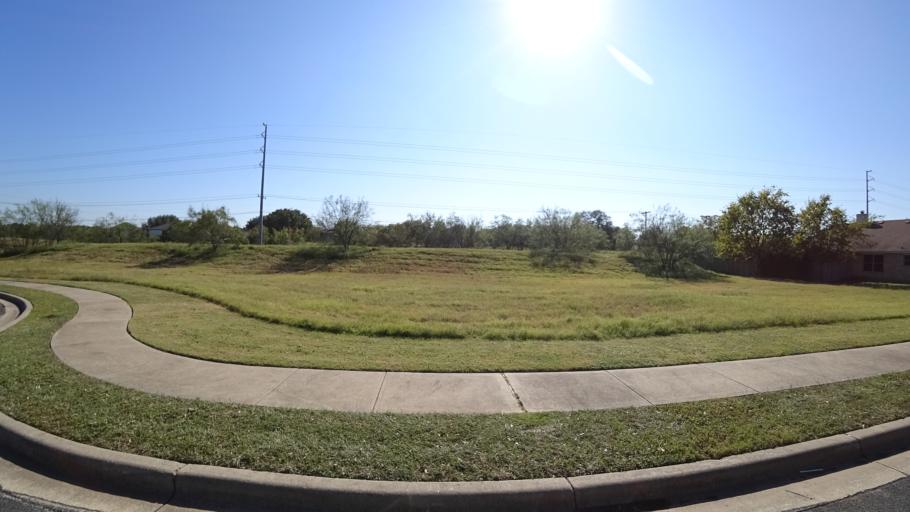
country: US
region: Texas
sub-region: Travis County
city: Shady Hollow
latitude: 30.1974
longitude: -97.8576
